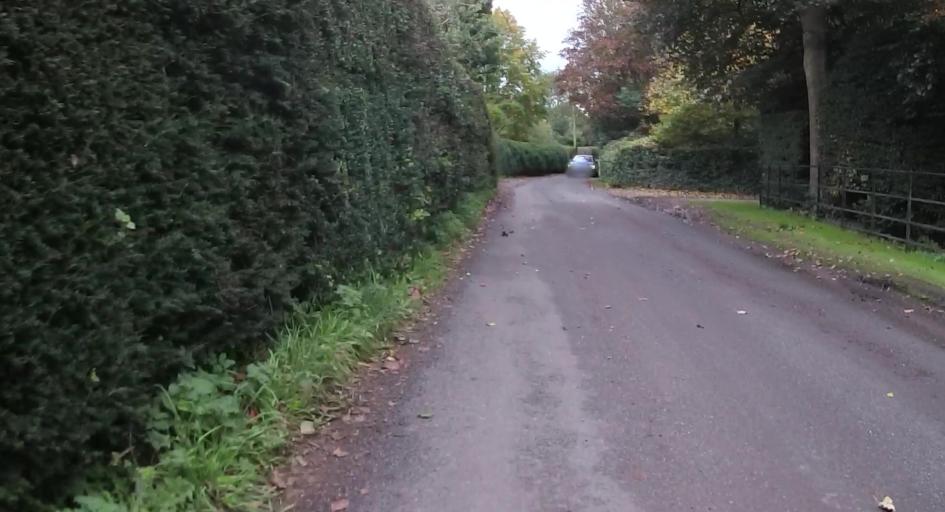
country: GB
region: England
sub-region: Hampshire
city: Four Marks
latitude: 51.1464
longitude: -1.1040
